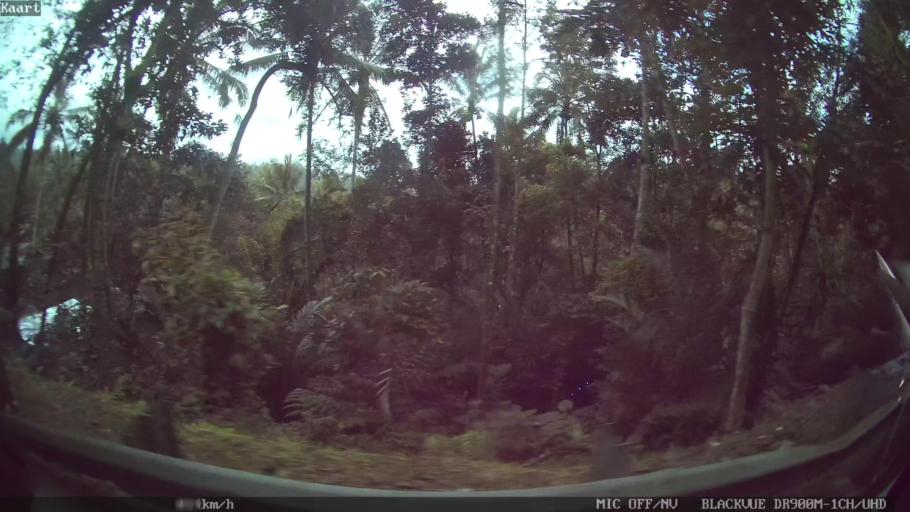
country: ID
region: Bali
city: Banjar Kubu
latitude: -8.4079
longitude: 115.4240
